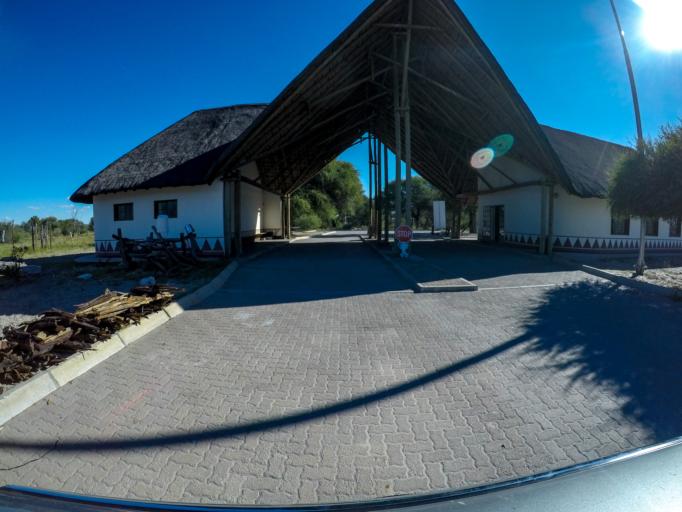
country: BW
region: Central
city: Rakops
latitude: -20.4721
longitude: 24.5178
